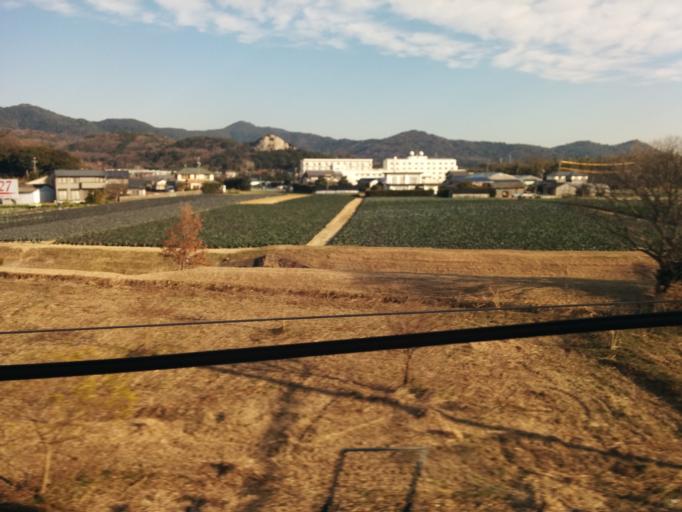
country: JP
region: Shizuoka
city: Kosai-shi
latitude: 34.7185
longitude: 137.4689
